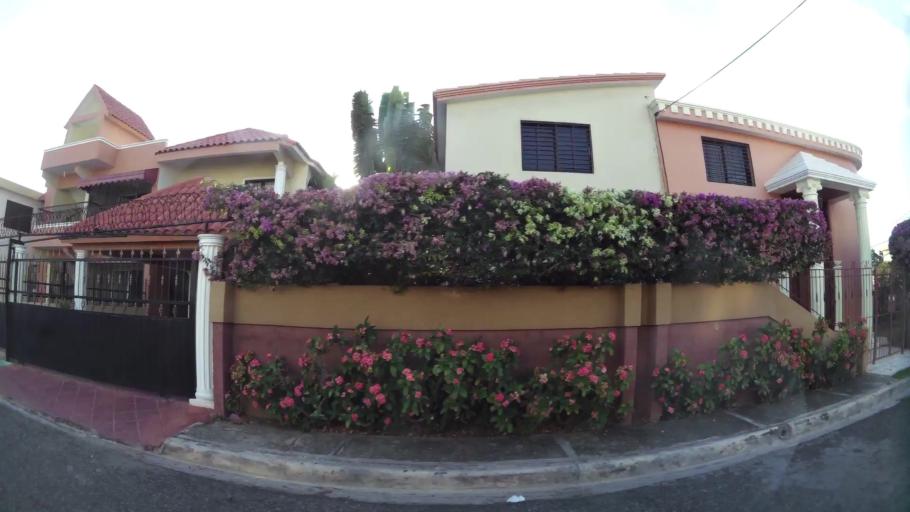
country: DO
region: Santo Domingo
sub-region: Santo Domingo
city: Santo Domingo Este
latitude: 18.4801
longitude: -69.8327
